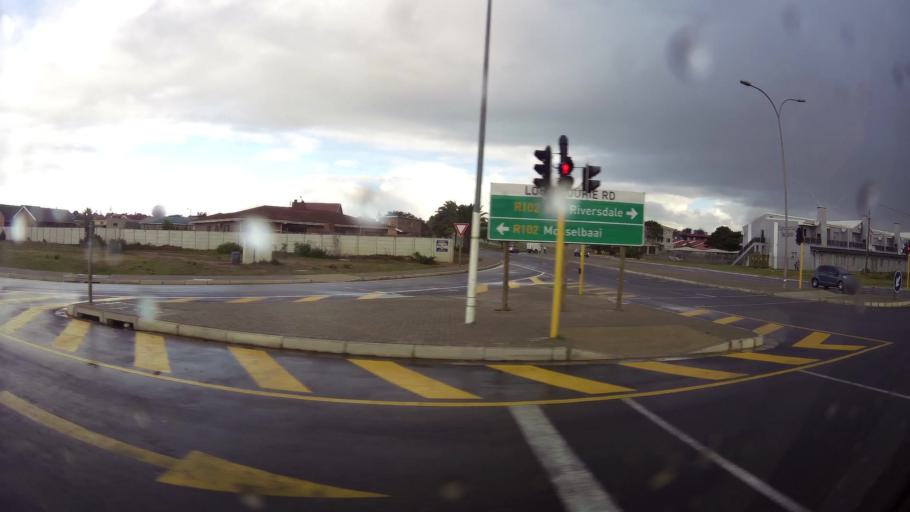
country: ZA
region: Western Cape
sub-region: Eden District Municipality
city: Mossel Bay
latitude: -34.1830
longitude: 22.1023
